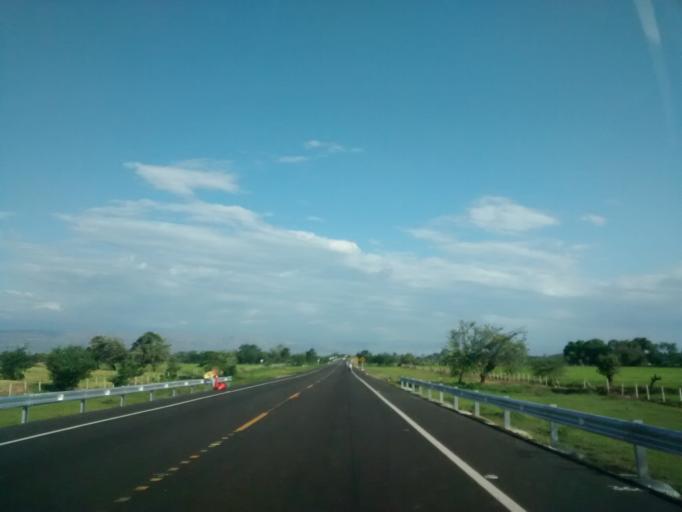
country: CO
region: Tolima
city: Espinal
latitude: 4.1512
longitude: -74.9141
